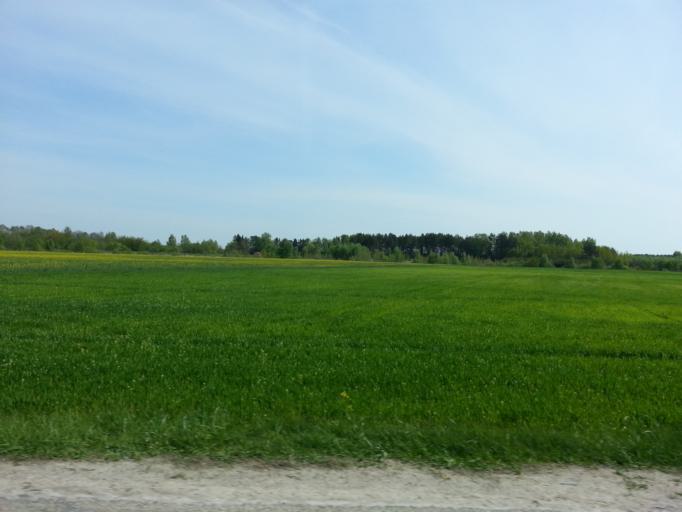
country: LT
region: Panevezys
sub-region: Panevezys City
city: Panevezys
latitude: 55.8044
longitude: 24.2742
